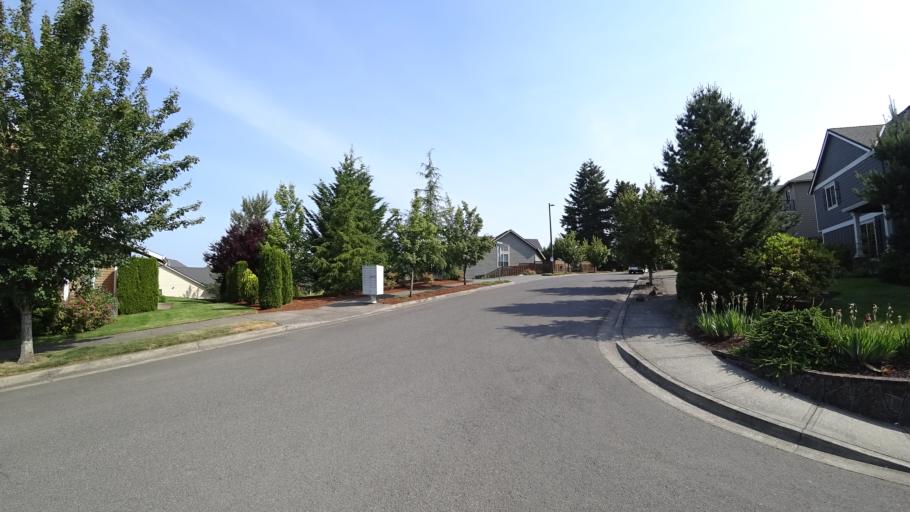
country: US
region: Oregon
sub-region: Clackamas County
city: Happy Valley
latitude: 45.4601
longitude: -122.5265
